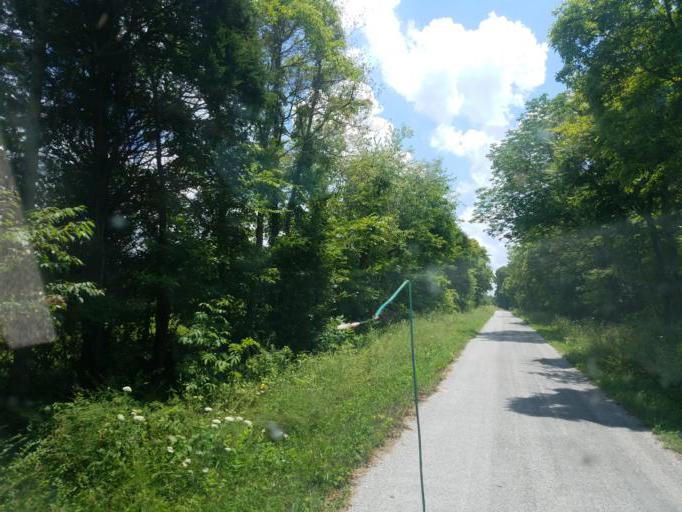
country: US
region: Kentucky
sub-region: Grayson County
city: Leitchfield
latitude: 37.4805
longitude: -86.4621
